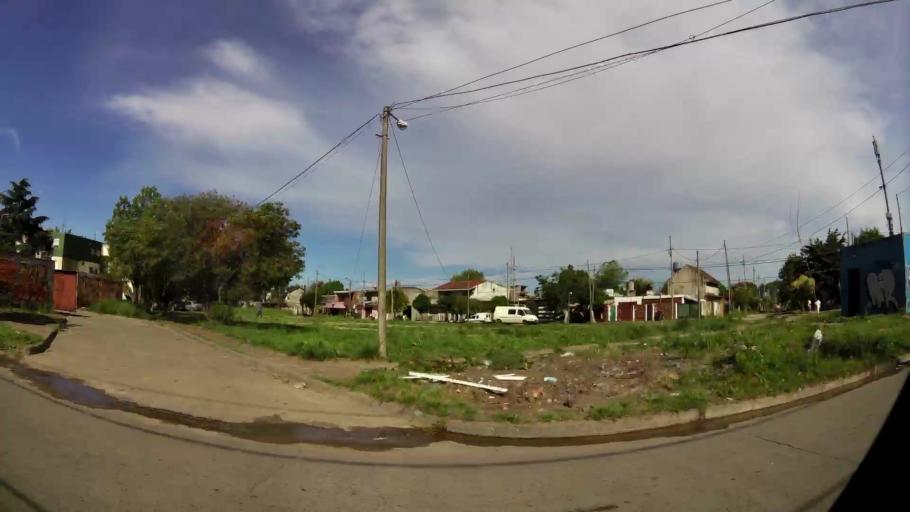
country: AR
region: Buenos Aires
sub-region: Partido de Almirante Brown
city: Adrogue
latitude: -34.8219
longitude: -58.3437
